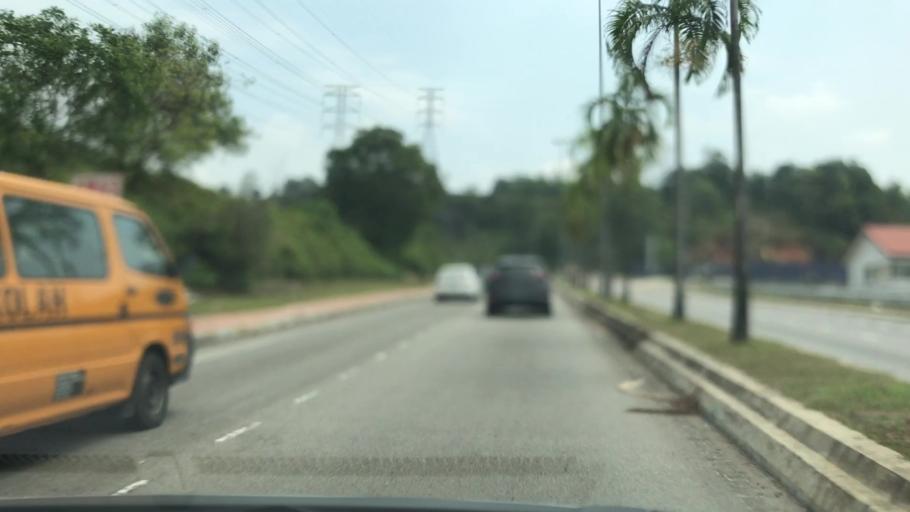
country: MY
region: Selangor
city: Kampong Baharu Balakong
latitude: 3.0388
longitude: 101.6758
